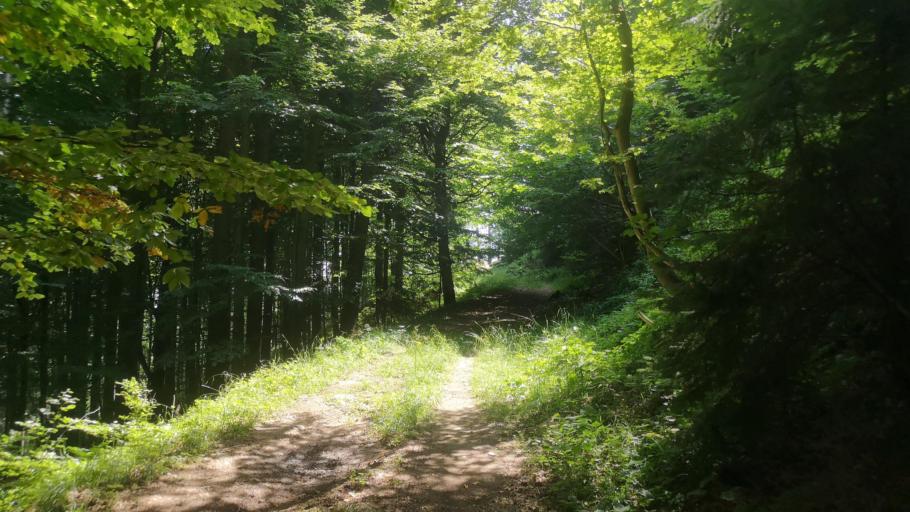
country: SK
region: Zilinsky
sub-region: Okres Zilina
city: Vrutky
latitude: 49.0946
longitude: 18.8545
